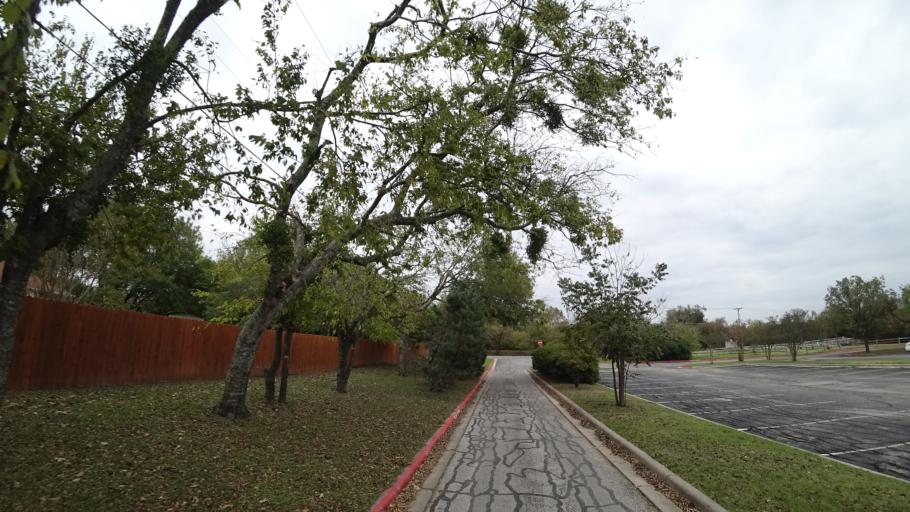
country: US
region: Texas
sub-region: Travis County
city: Pflugerville
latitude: 30.4454
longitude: -97.6188
